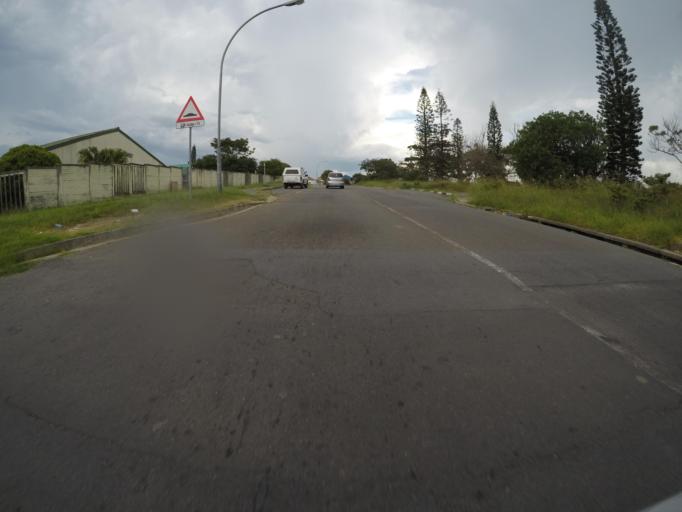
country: ZA
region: Eastern Cape
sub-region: Buffalo City Metropolitan Municipality
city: East London
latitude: -33.0237
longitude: 27.8592
